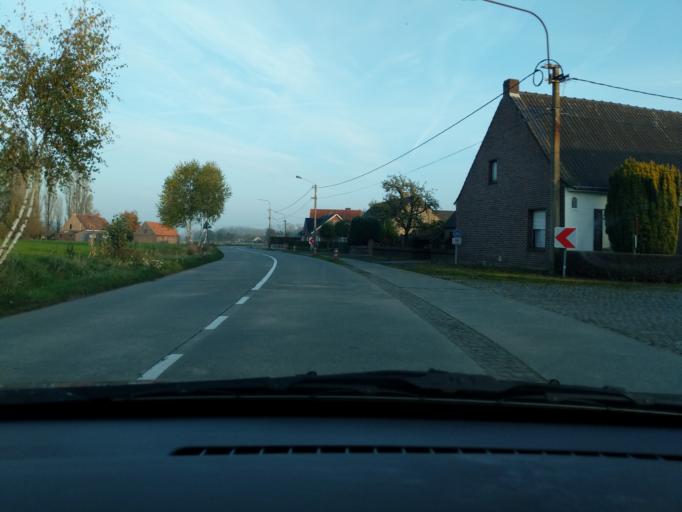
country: BE
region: Flanders
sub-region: Provincie Oost-Vlaanderen
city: Aalter
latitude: 51.0451
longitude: 3.4748
